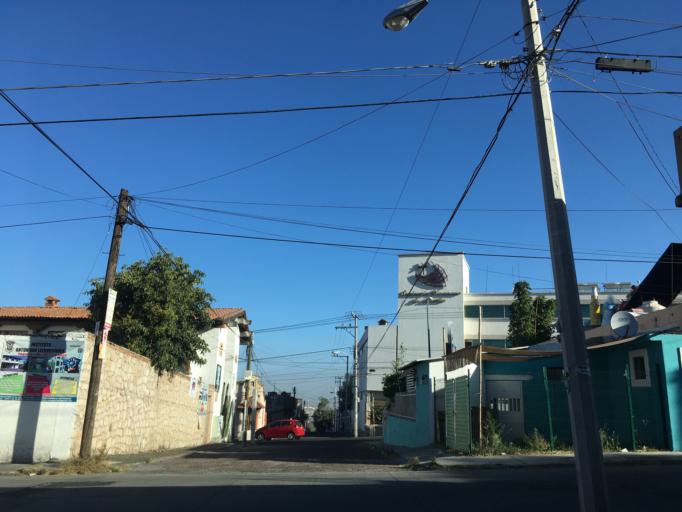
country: MX
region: Michoacan
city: Morelia
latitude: 19.6783
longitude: -101.1949
